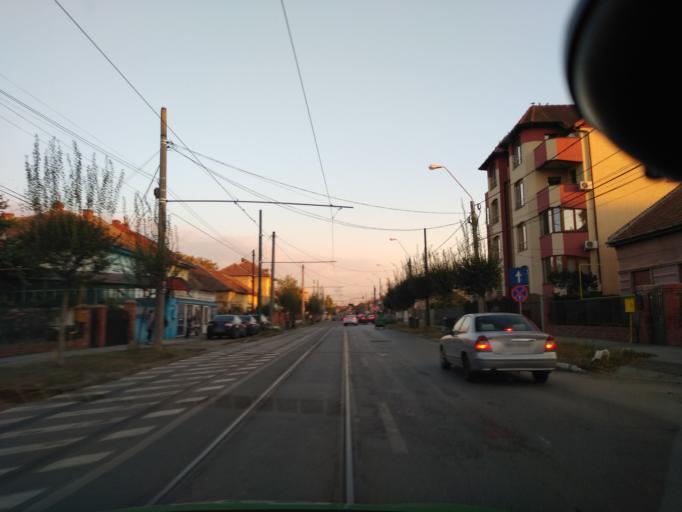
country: RO
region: Timis
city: Timisoara
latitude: 45.7336
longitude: 21.2273
